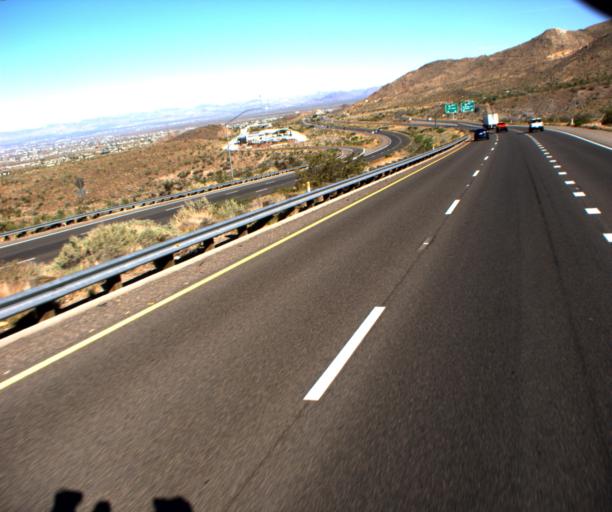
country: US
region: Arizona
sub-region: Mohave County
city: Kingman
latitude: 35.2153
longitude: -114.1150
